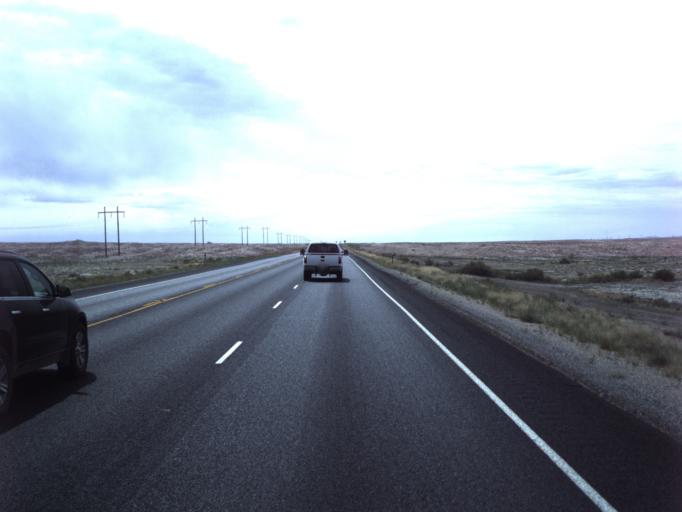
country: US
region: Utah
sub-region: Carbon County
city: East Carbon City
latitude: 39.2050
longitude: -110.3386
